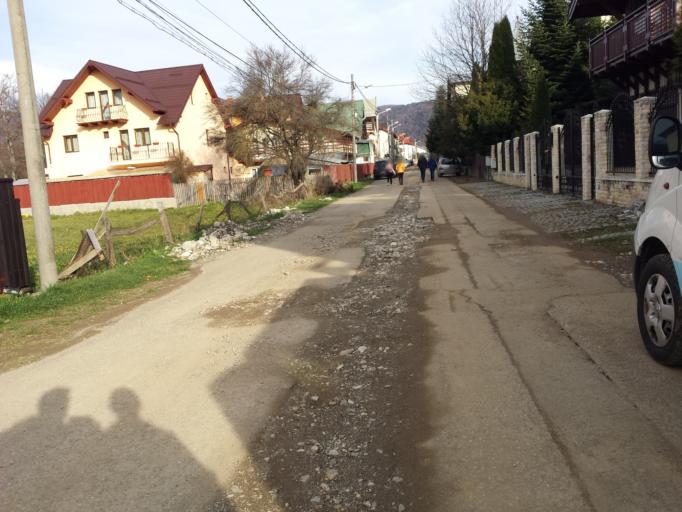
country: RO
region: Prahova
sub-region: Oras Busteni
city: Busteni
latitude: 45.4079
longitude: 25.5404
